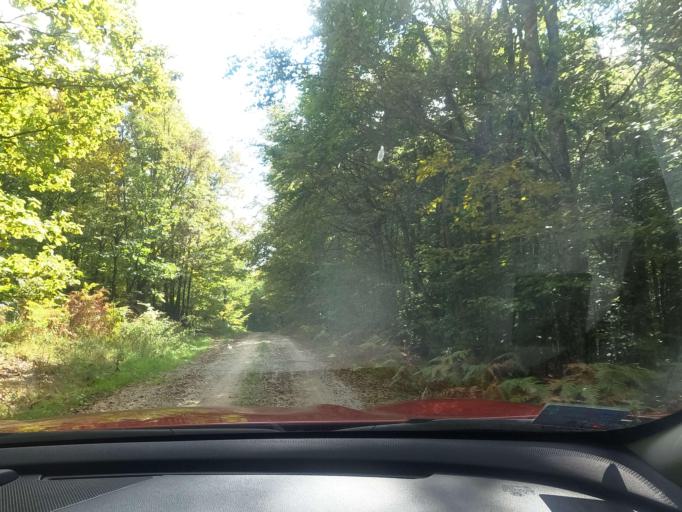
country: BA
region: Federation of Bosnia and Herzegovina
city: Velika Kladusa
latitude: 45.2617
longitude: 15.7842
